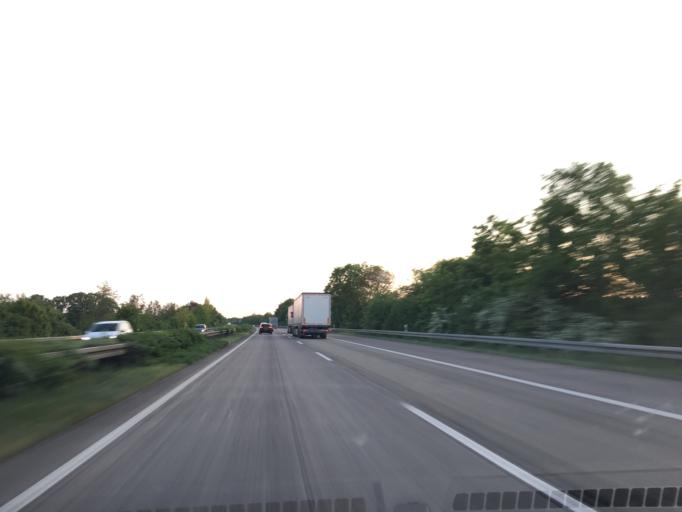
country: DE
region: North Rhine-Westphalia
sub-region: Regierungsbezirk Munster
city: Ladbergen
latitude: 52.1665
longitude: 7.7559
